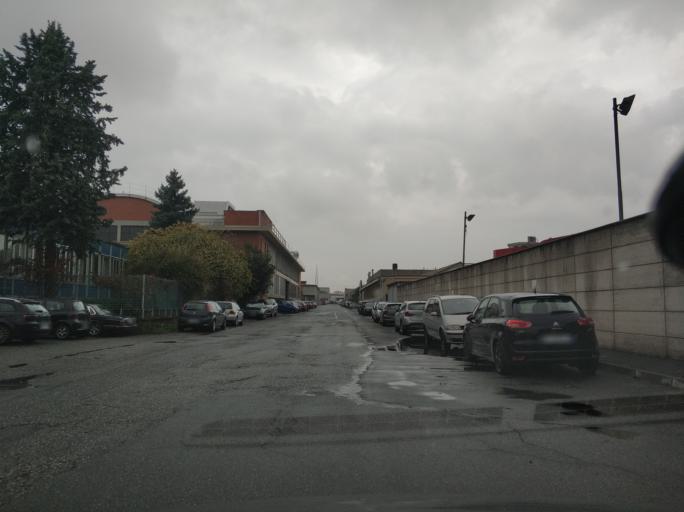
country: IT
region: Piedmont
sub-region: Provincia di Torino
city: Settimo Torinese
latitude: 45.1204
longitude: 7.7481
